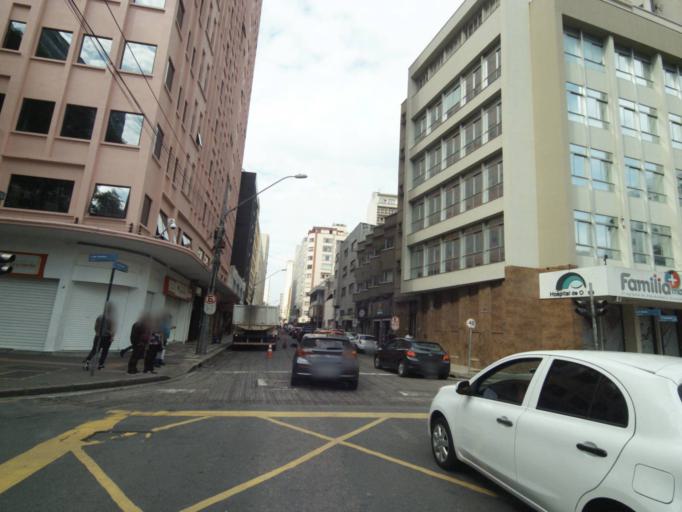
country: BR
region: Parana
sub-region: Curitiba
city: Curitiba
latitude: -25.4325
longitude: -49.2722
